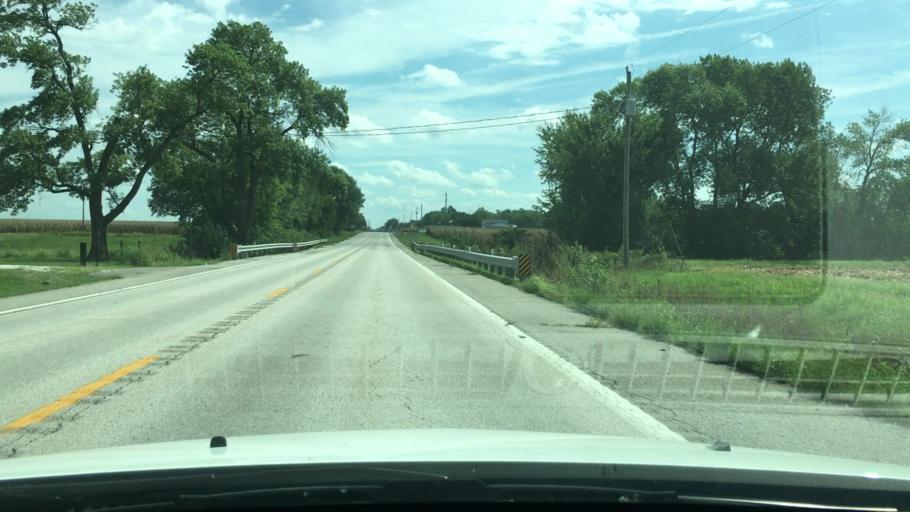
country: US
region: Missouri
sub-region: Audrain County
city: Vandalia
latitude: 39.2795
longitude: -91.5846
